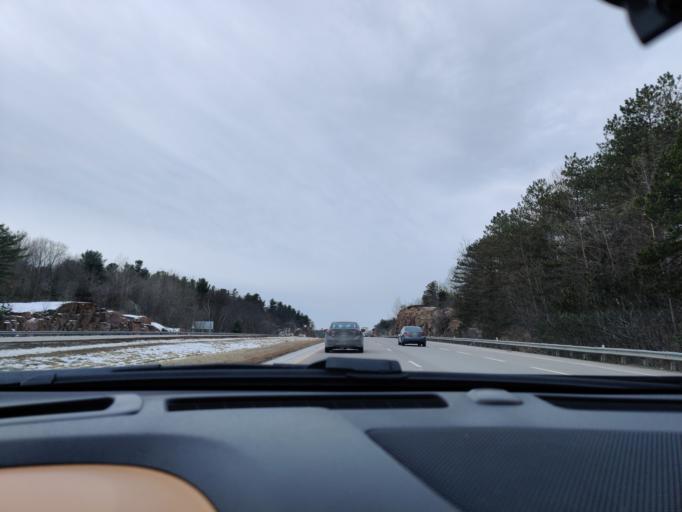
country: US
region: New York
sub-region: Jefferson County
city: Alexandria Bay
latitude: 44.3781
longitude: -76.0116
